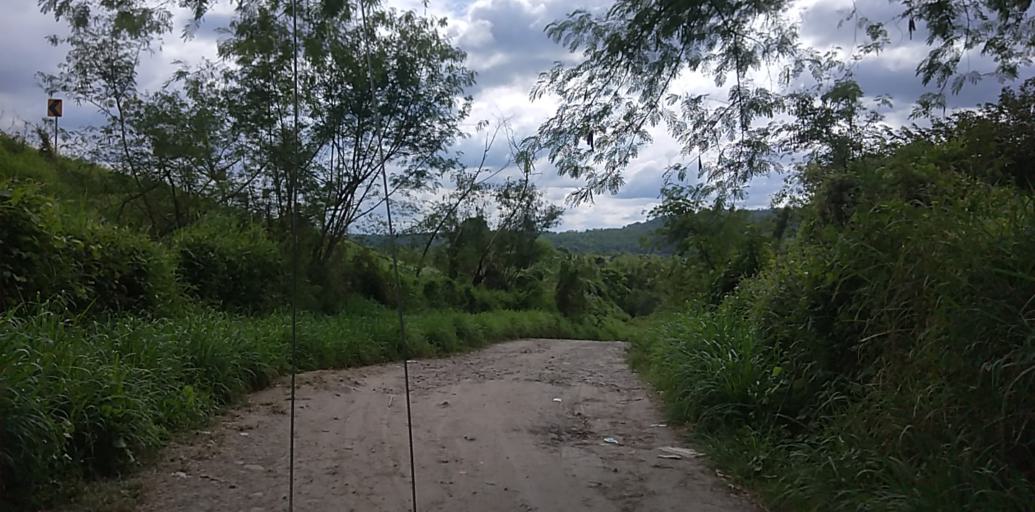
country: PH
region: Central Luzon
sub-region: Province of Pampanga
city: Dolores
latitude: 15.1152
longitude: 120.5050
